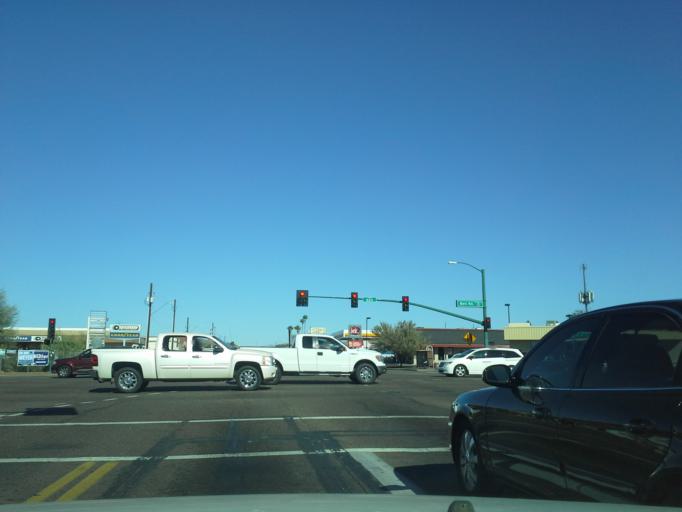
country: US
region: Arizona
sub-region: Maricopa County
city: Paradise Valley
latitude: 33.6402
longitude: -112.0309
